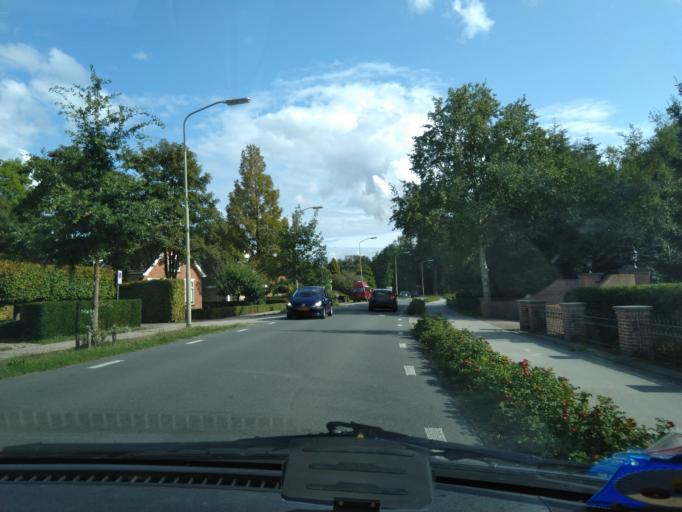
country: NL
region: Groningen
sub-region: Gemeente Groningen
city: Groningen
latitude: 53.1689
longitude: 6.5531
